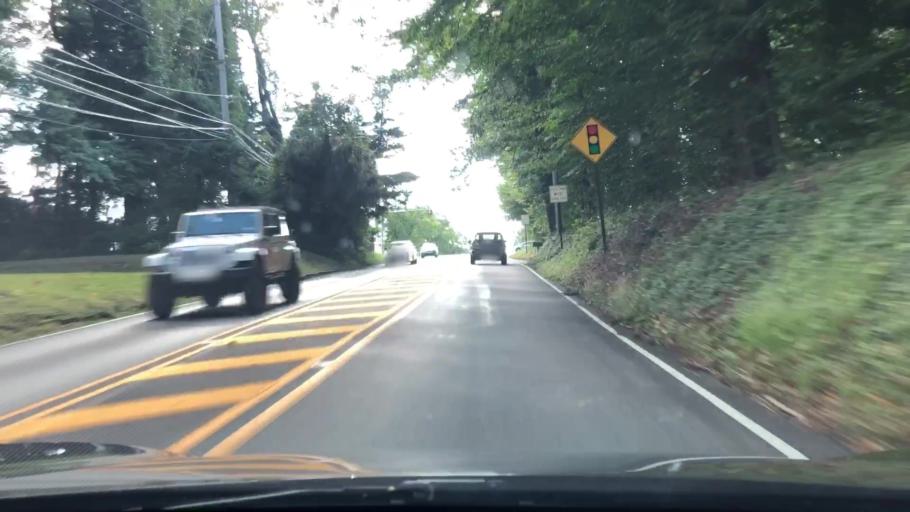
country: US
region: Pennsylvania
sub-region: Chester County
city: West Chester
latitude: 39.9213
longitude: -75.5737
